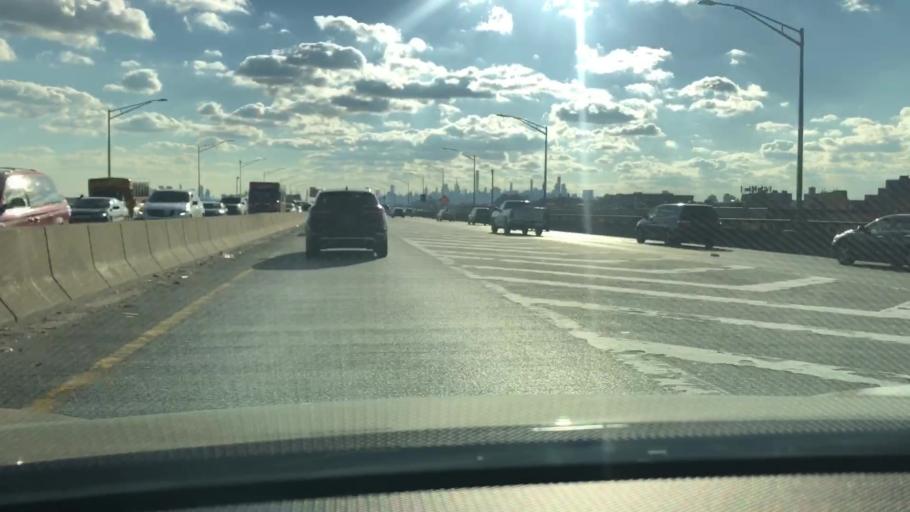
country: US
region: New York
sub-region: Bronx
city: The Bronx
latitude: 40.8186
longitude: -73.8920
